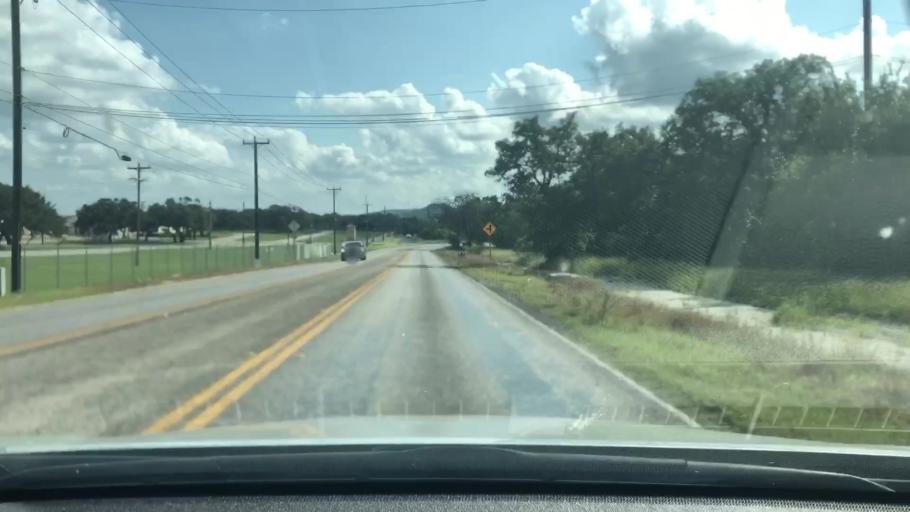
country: US
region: Texas
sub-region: Bexar County
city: Cross Mountain
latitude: 29.6813
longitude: -98.6316
